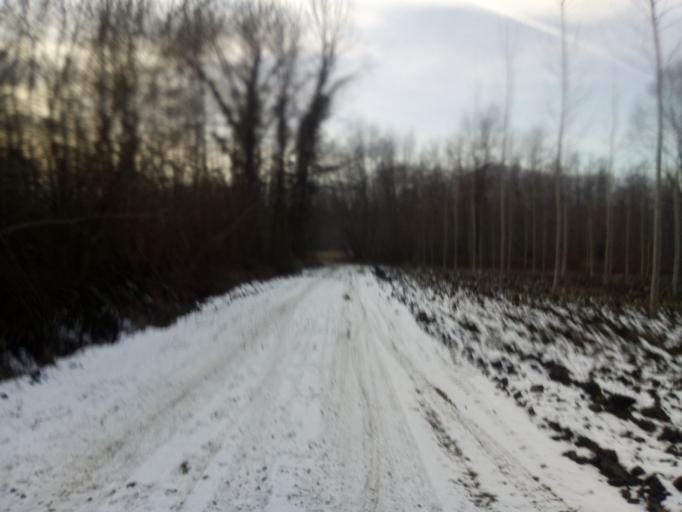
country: IT
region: Piedmont
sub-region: Provincia di Torino
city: Cascinette d'Ivrea
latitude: 45.4858
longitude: 7.9158
